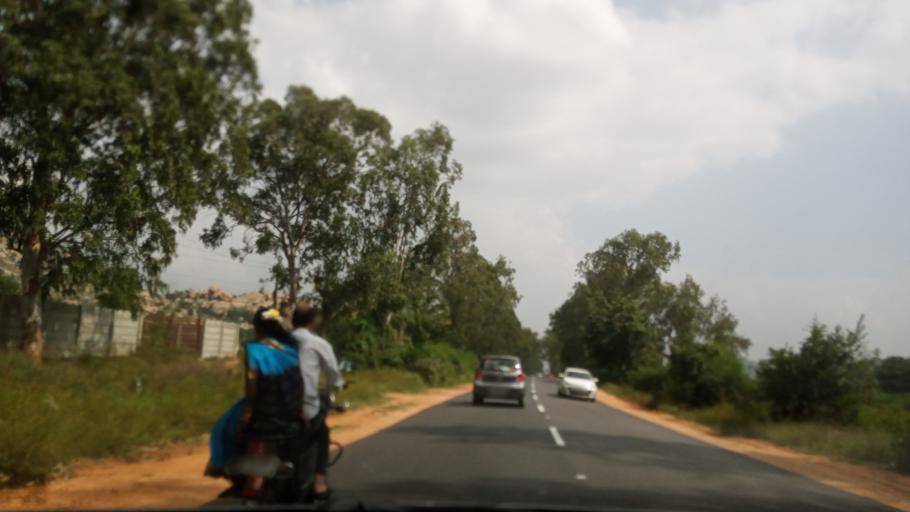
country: IN
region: Andhra Pradesh
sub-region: Chittoor
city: Madanapalle
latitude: 13.6358
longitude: 78.6034
